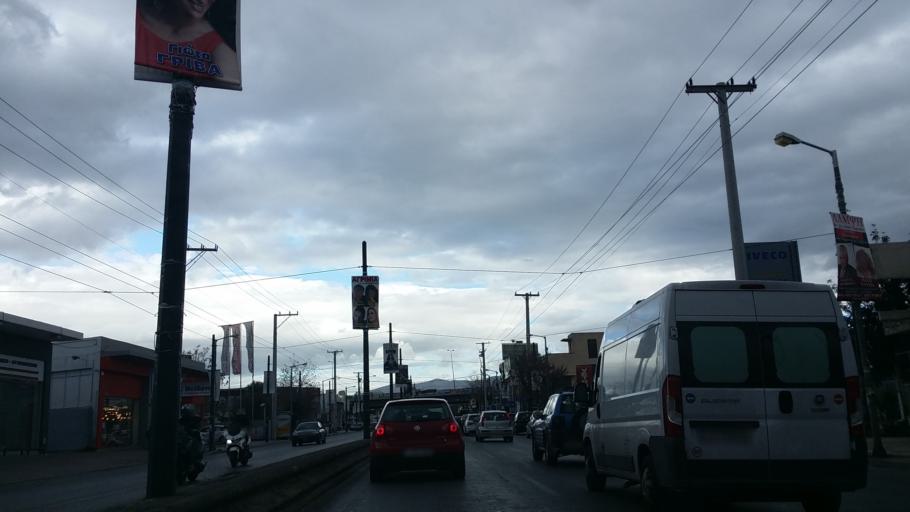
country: GR
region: Attica
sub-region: Nomarchia Athinas
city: Aigaleo
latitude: 37.9762
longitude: 23.6742
